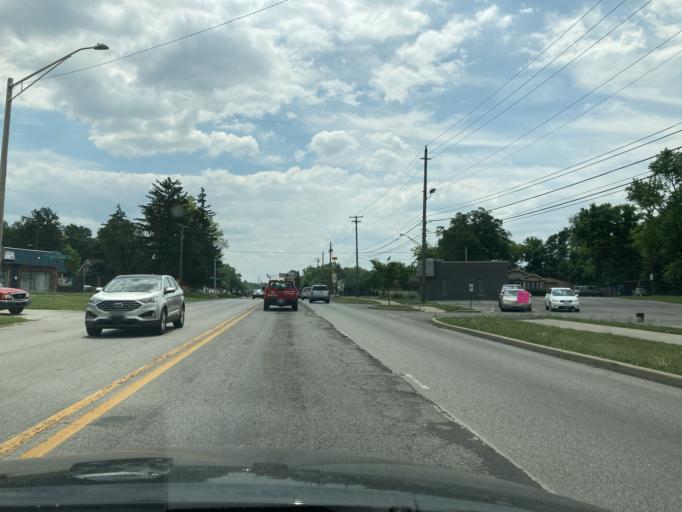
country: US
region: Indiana
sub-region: Marion County
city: Meridian Hills
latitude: 39.8604
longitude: -86.1981
